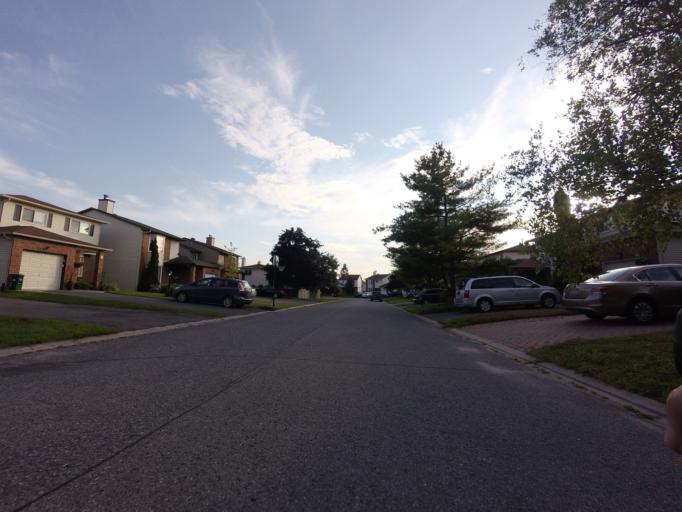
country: CA
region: Ontario
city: Bells Corners
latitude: 45.2785
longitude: -75.7766
